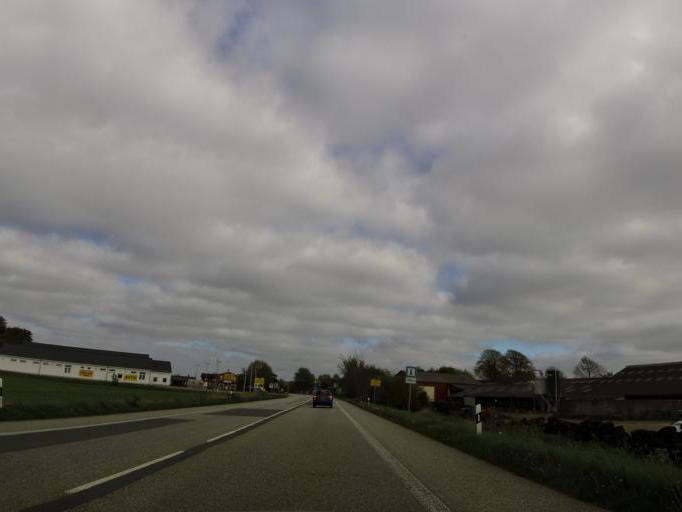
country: DE
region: Schleswig-Holstein
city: Risum-Lindholm
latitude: 54.7630
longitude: 8.8730
